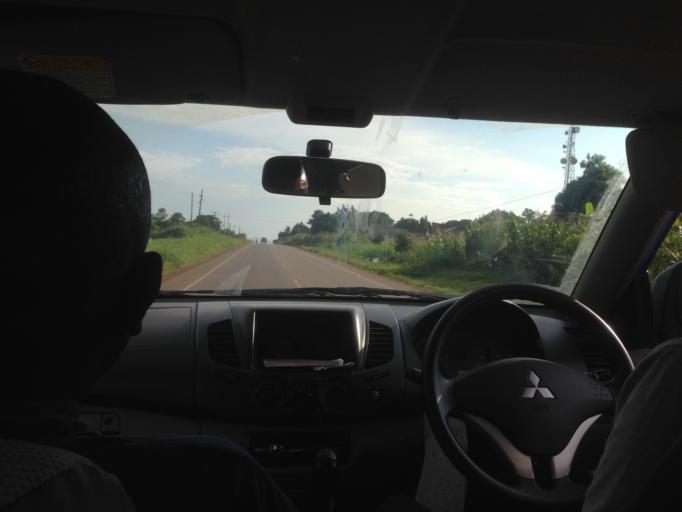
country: UG
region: Western Region
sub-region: Kiryandongo District
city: Kiryandongo
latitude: 1.8657
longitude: 32.0498
